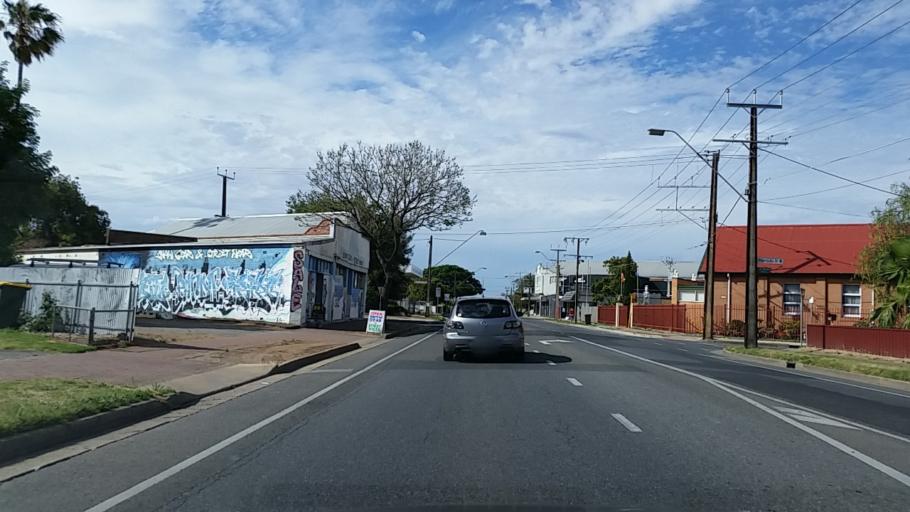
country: AU
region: South Australia
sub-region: Charles Sturt
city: Woodville
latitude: -34.8844
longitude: 138.5492
